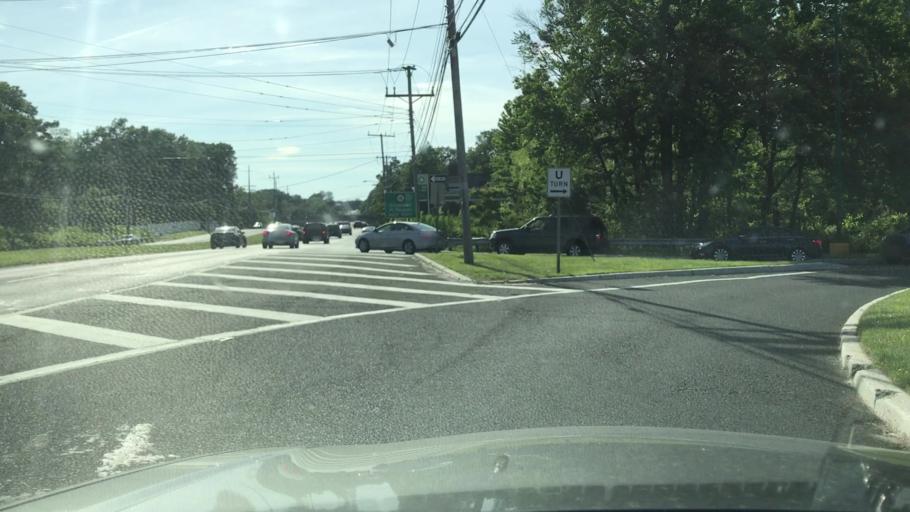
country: US
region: New Jersey
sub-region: Monmouth County
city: Wanamassa
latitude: 40.2278
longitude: -74.0453
